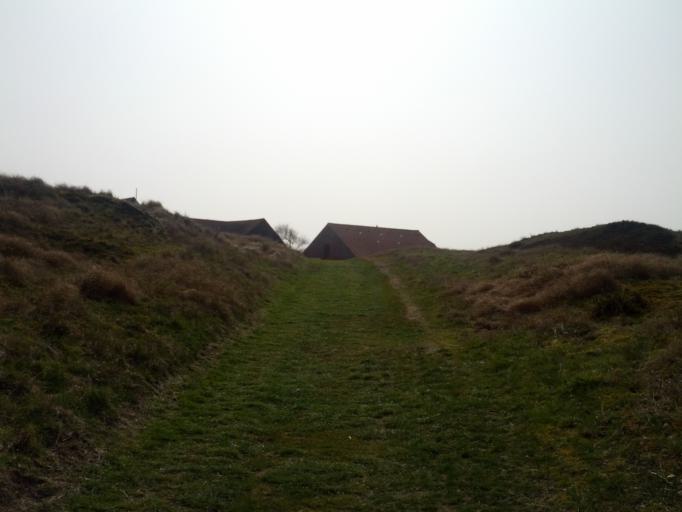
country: DE
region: Lower Saxony
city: Spiekeroog
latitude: 53.7509
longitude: 7.5935
